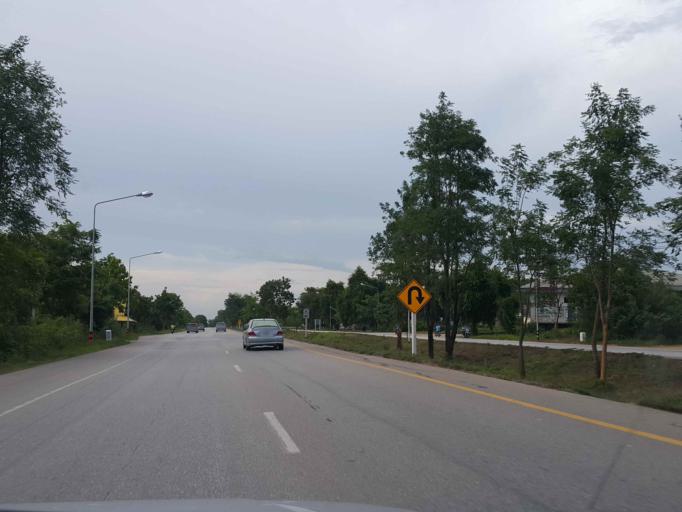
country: TH
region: Lampang
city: Ko Kha
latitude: 18.1644
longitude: 99.4049
